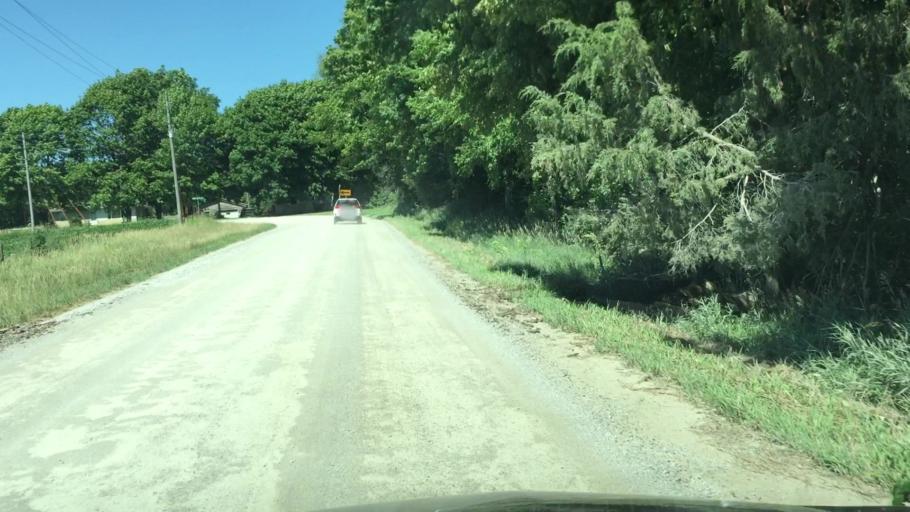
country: US
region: Iowa
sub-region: Linn County
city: Ely
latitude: 41.8329
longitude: -91.5883
